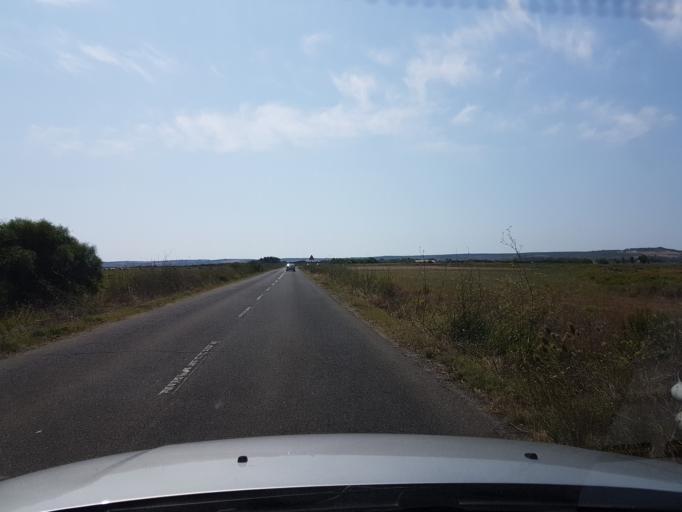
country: IT
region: Sardinia
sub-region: Provincia di Oristano
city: Cabras
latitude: 39.9166
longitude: 8.4843
